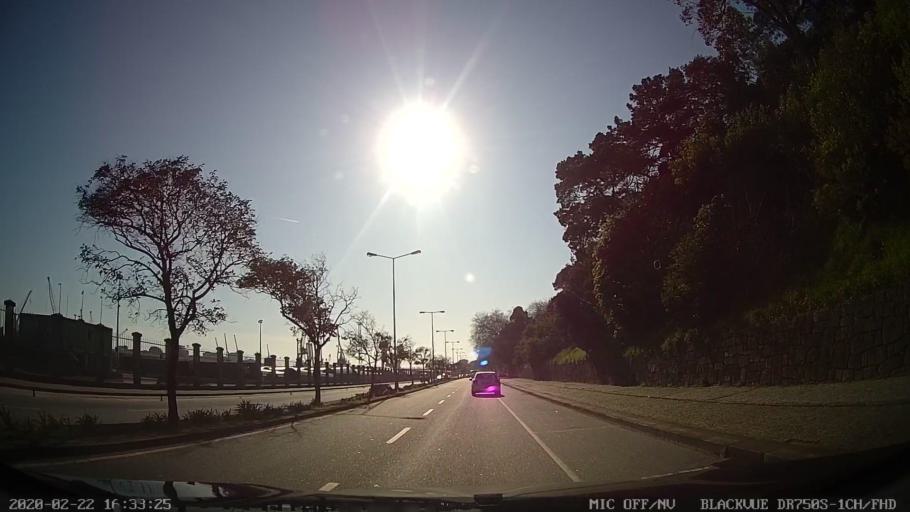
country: PT
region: Porto
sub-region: Matosinhos
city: Leca da Palmeira
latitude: 41.1931
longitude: -8.6898
